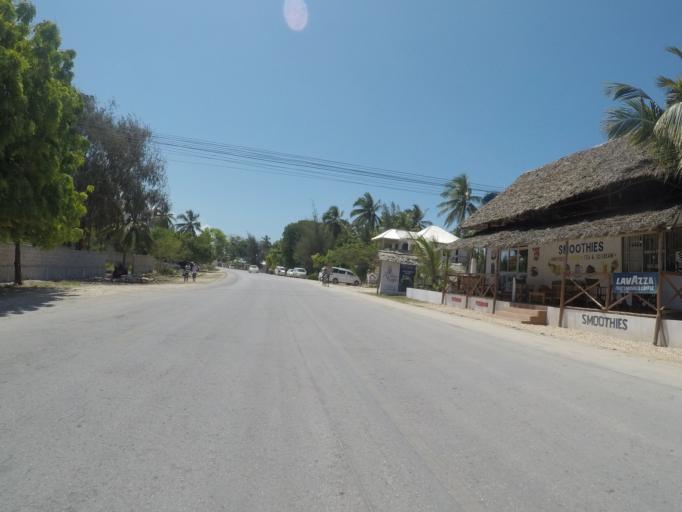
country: TZ
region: Zanzibar Central/South
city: Nganane
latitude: -6.2691
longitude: 39.5325
